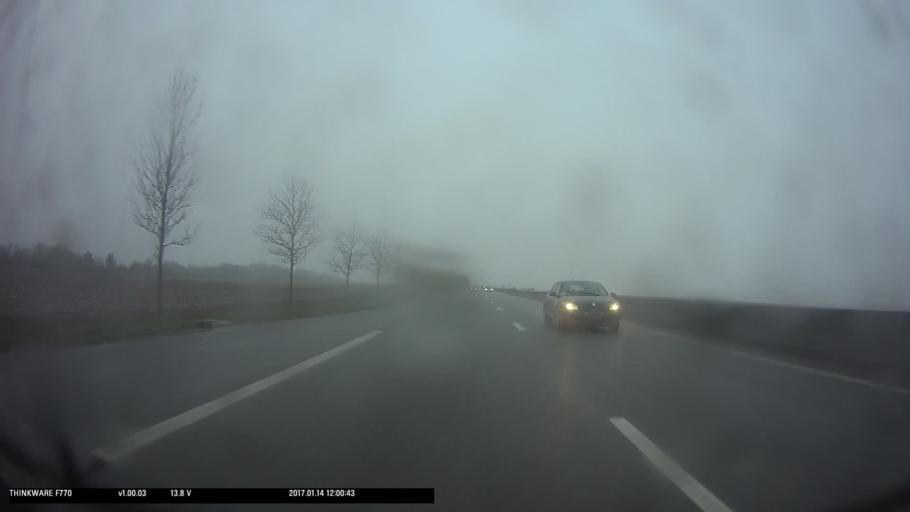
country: FR
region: Ile-de-France
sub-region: Departement du Val-d'Oise
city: Vigny
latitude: 49.0779
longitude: 1.9430
